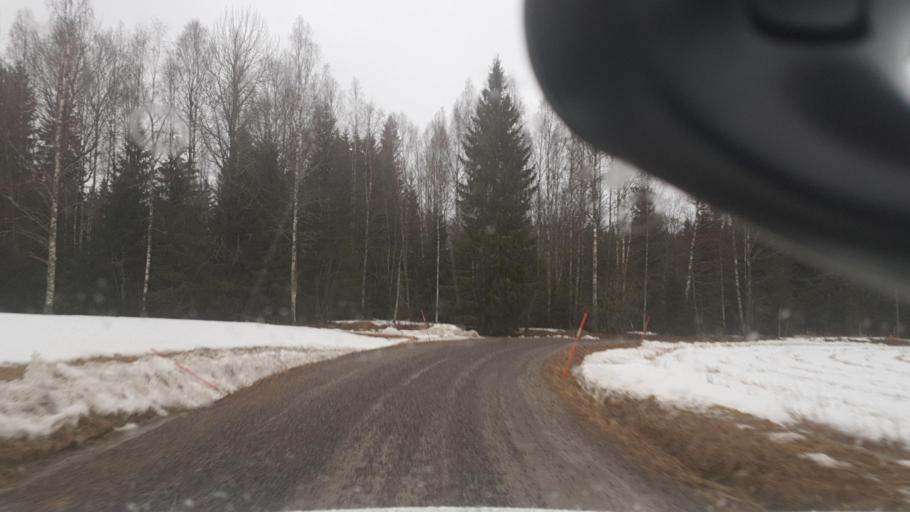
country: SE
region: Vaermland
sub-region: Eda Kommun
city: Charlottenberg
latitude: 59.8376
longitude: 12.3559
